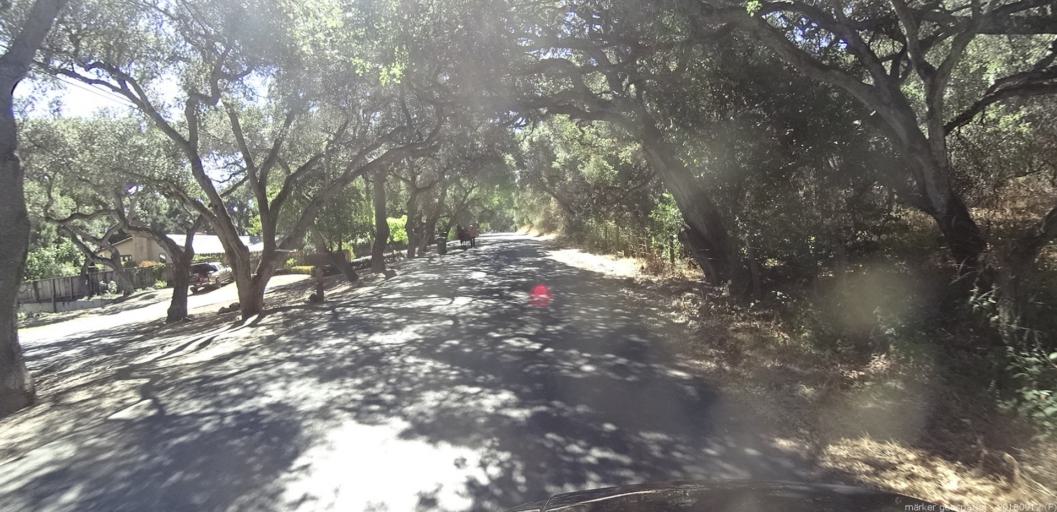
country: US
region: California
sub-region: Monterey County
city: Carmel Valley Village
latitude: 36.4853
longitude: -121.7471
